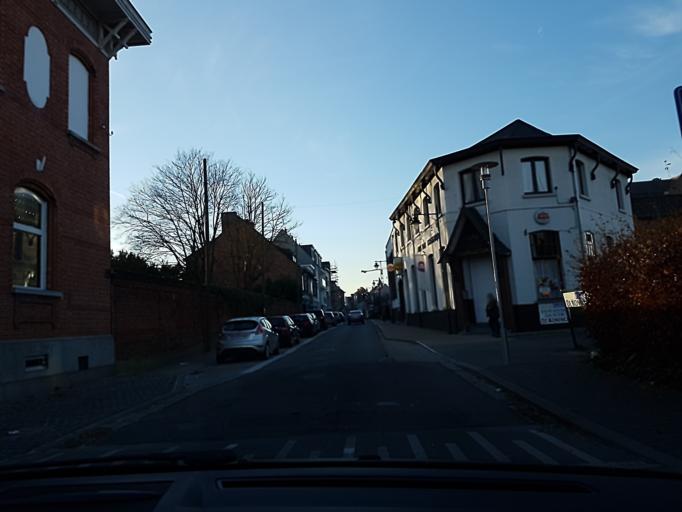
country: BE
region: Flanders
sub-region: Provincie Antwerpen
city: Bornem
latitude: 51.0996
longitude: 4.2395
